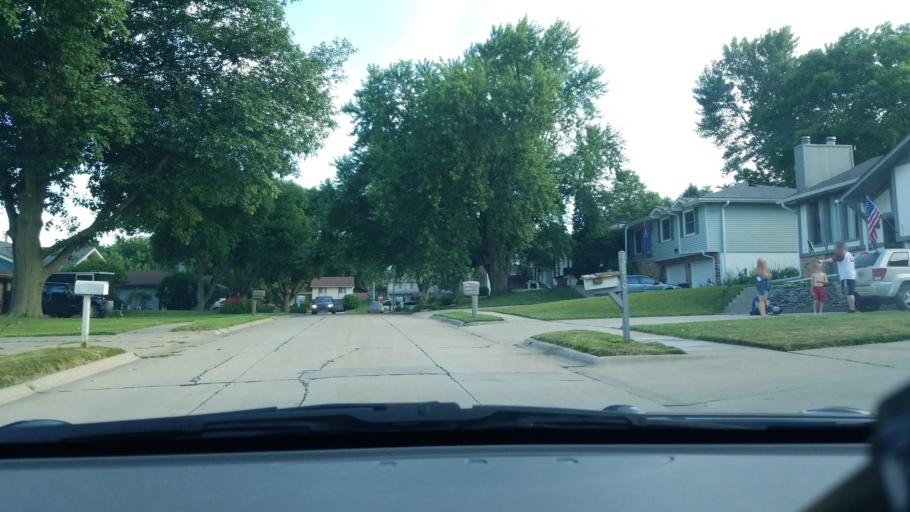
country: US
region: Nebraska
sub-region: Sarpy County
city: Offutt Air Force Base
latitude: 41.1162
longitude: -95.9526
